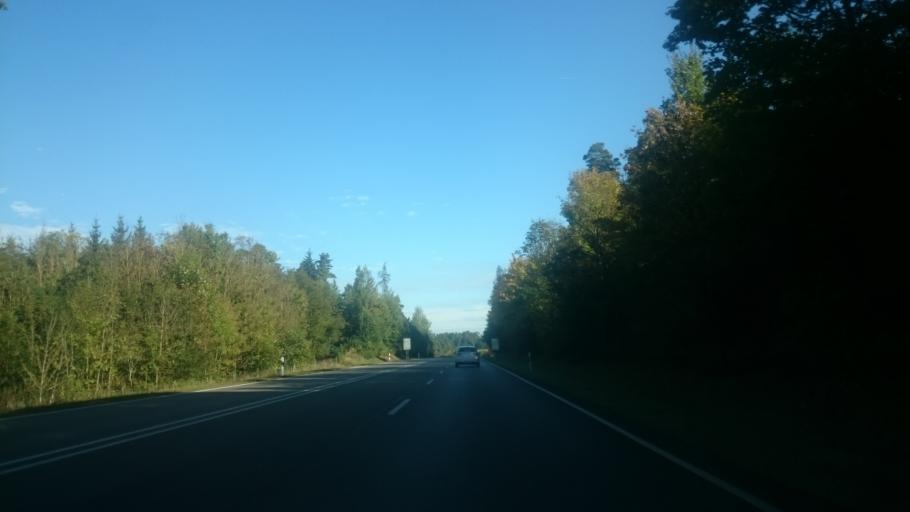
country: DE
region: Bavaria
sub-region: Regierungsbezirk Mittelfranken
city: Pleinfeld
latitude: 49.0885
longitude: 10.9800
